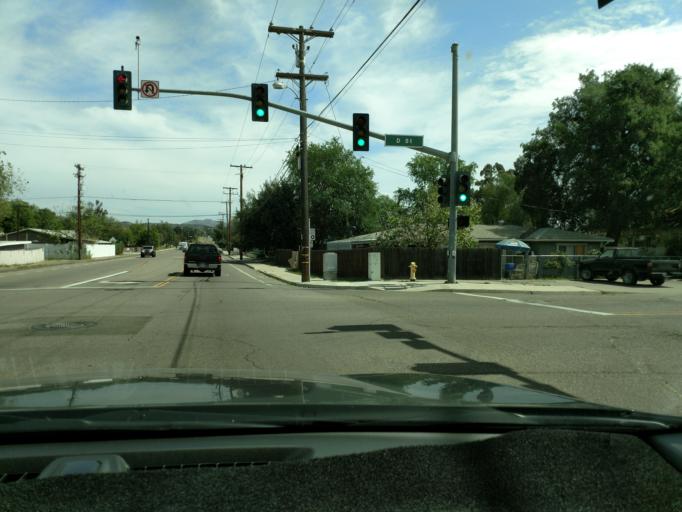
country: US
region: California
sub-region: San Diego County
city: Ramona
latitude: 33.0412
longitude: -116.8680
